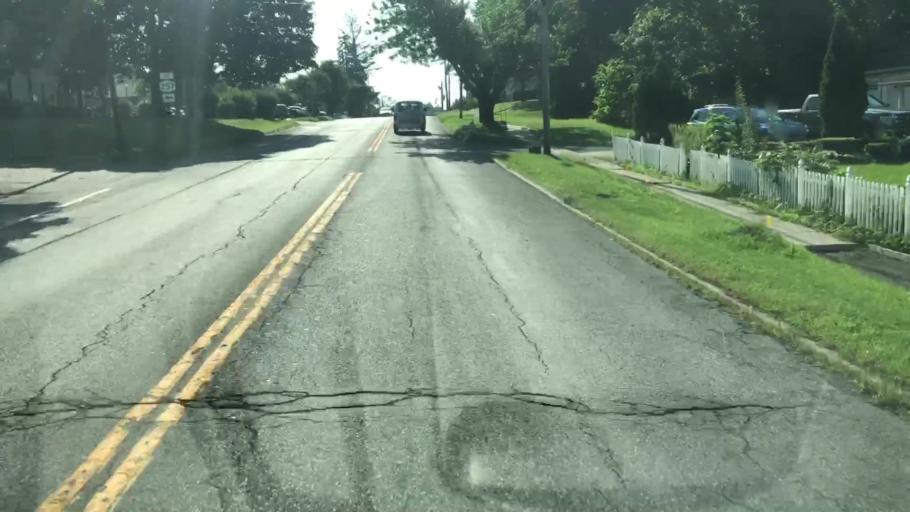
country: US
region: New York
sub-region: Onondaga County
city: Manlius
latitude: 43.0074
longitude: -75.9881
